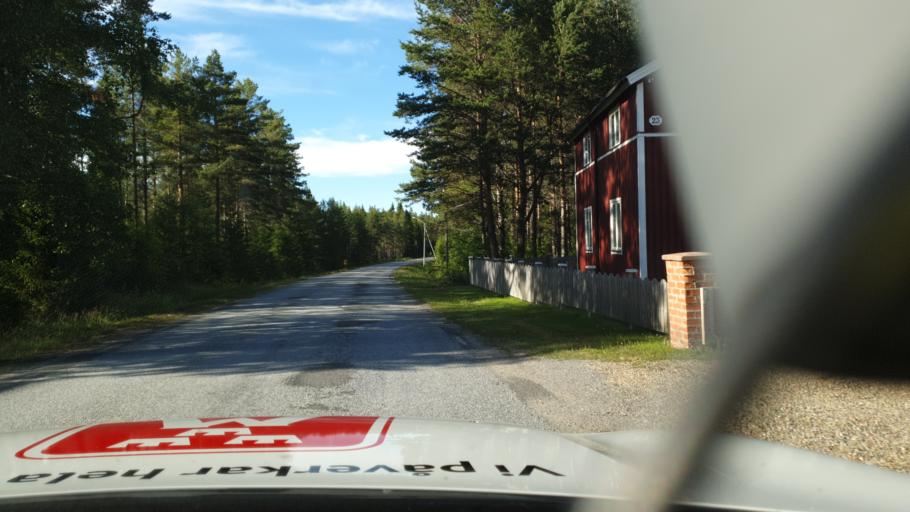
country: SE
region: Vaesterbotten
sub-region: Umea Kommun
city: Saevar
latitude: 63.9169
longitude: 20.7652
